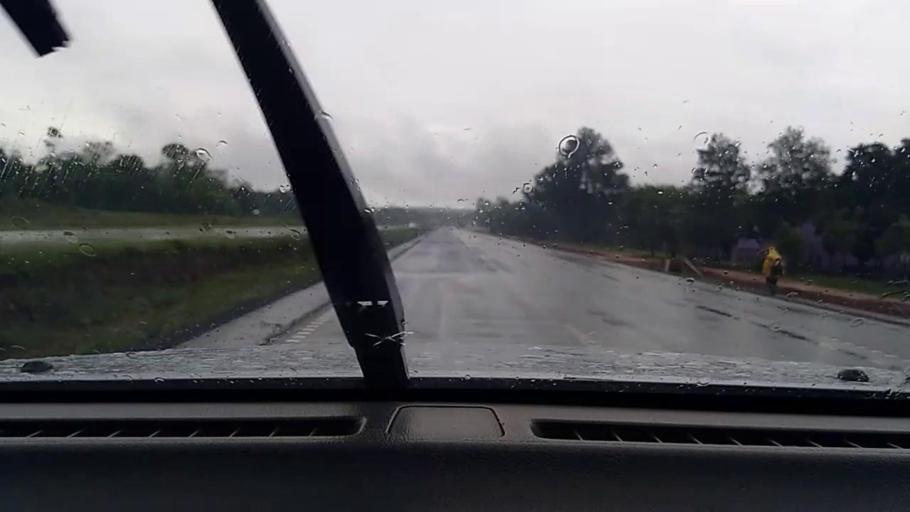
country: PY
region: Caaguazu
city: Repatriacion
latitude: -25.4633
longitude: -55.9288
